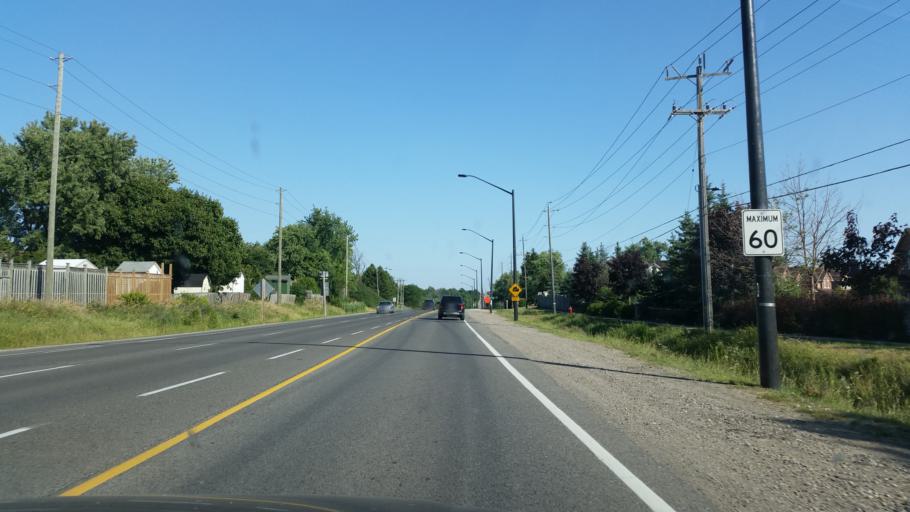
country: CA
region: Ontario
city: Brampton
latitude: 43.8867
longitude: -79.7481
